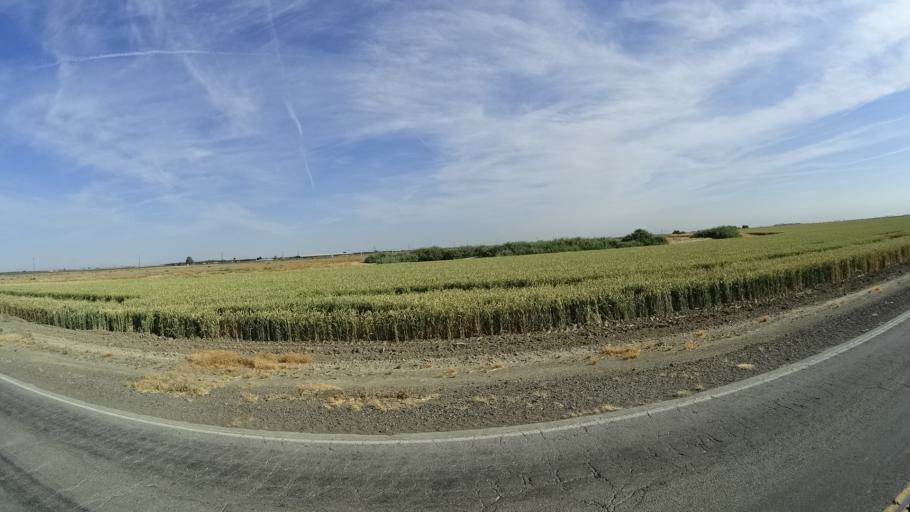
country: US
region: California
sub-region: Kings County
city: Home Garden
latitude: 36.3430
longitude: -119.5347
